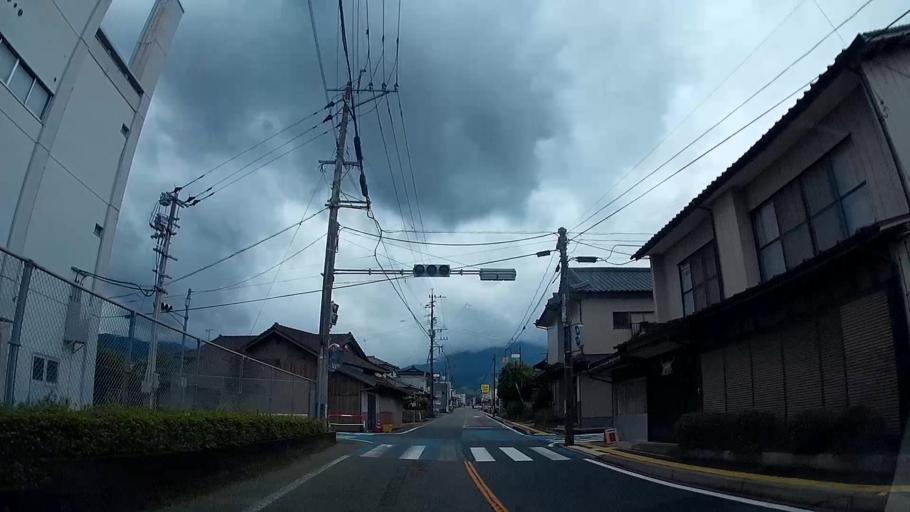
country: JP
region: Kumamoto
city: Aso
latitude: 32.9462
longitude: 131.1179
